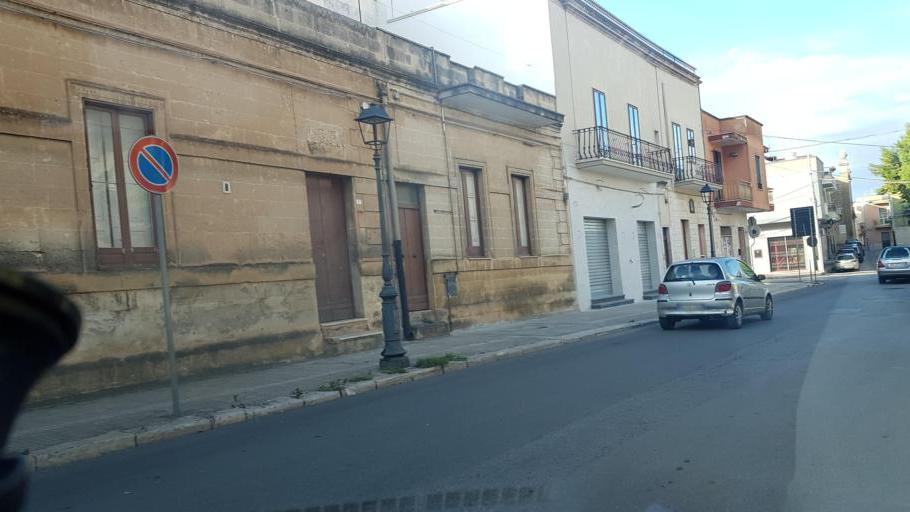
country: IT
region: Apulia
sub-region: Provincia di Brindisi
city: Francavilla Fontana
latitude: 40.5324
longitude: 17.5860
